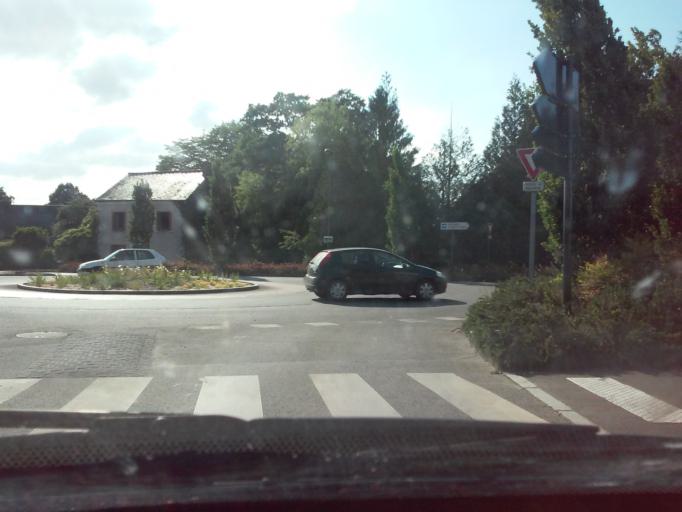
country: FR
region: Brittany
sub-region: Departement d'Ille-et-Vilaine
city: Liffre
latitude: 48.2058
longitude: -1.5209
